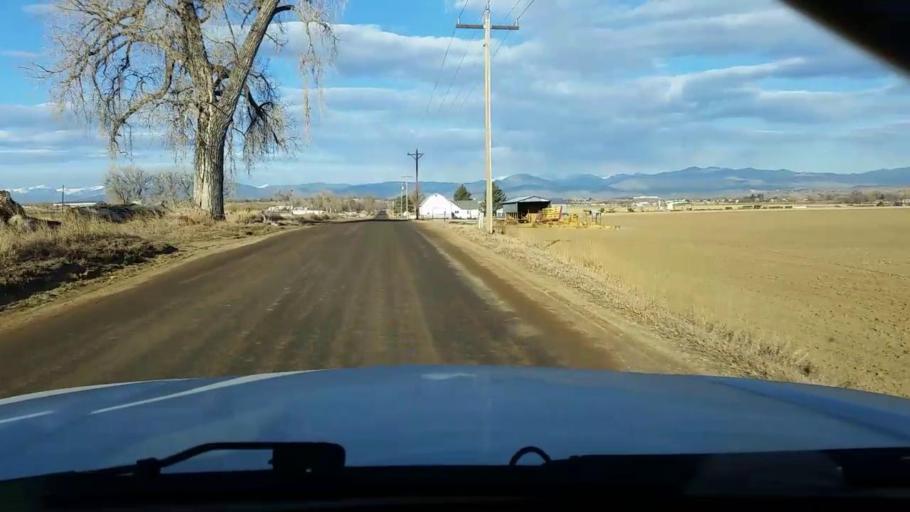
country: US
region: Colorado
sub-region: Larimer County
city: Campion
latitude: 40.3710
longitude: -105.0452
